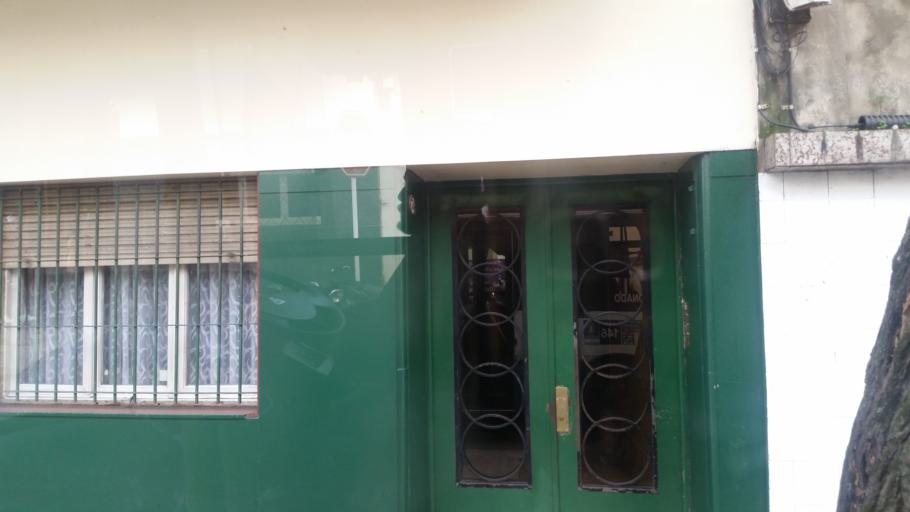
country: AR
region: Buenos Aires F.D.
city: Buenos Aires
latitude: -34.6071
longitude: -58.4187
